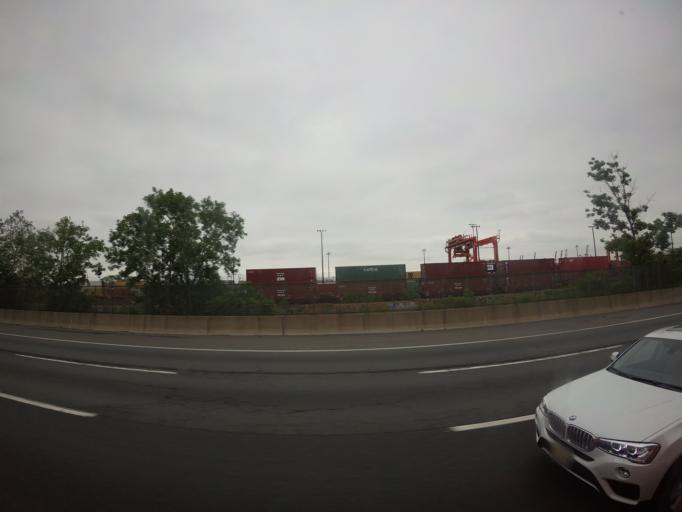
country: US
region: New Jersey
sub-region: Essex County
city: Newark
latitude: 40.6967
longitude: -74.1571
